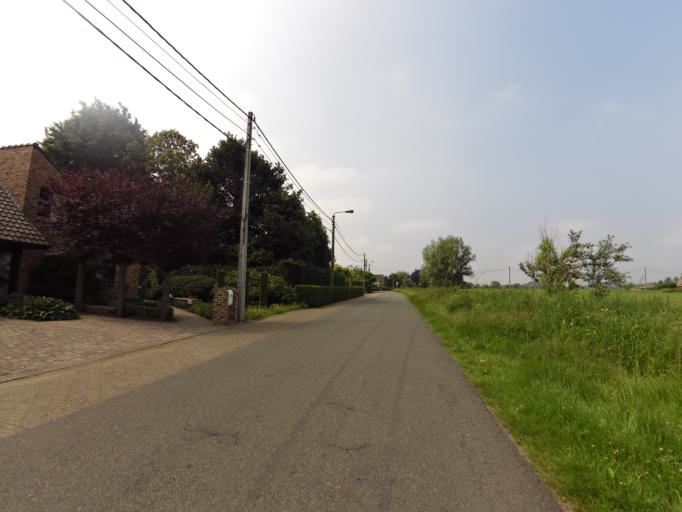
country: BE
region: Flanders
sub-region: Provincie West-Vlaanderen
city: Ichtegem
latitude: 51.1163
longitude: 3.0673
